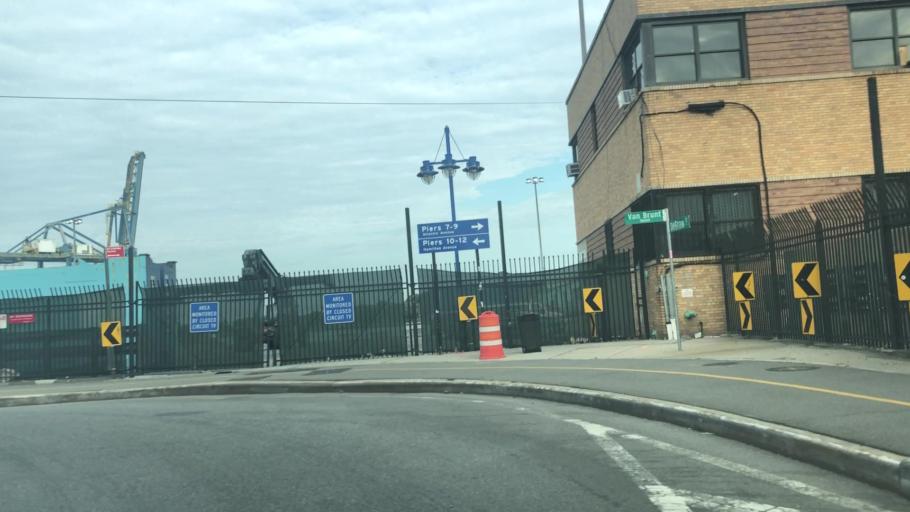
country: US
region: New York
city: New York City
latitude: 40.6863
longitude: -74.0044
